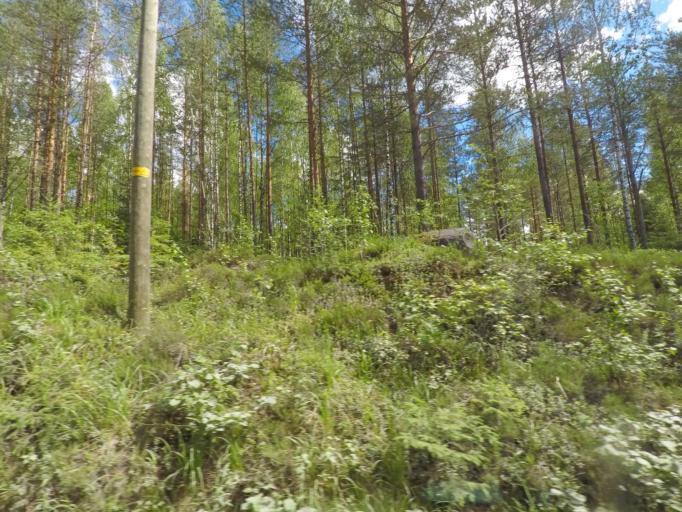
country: FI
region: Central Finland
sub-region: Jyvaeskylae
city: Hankasalmi
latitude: 62.4332
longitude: 26.6484
